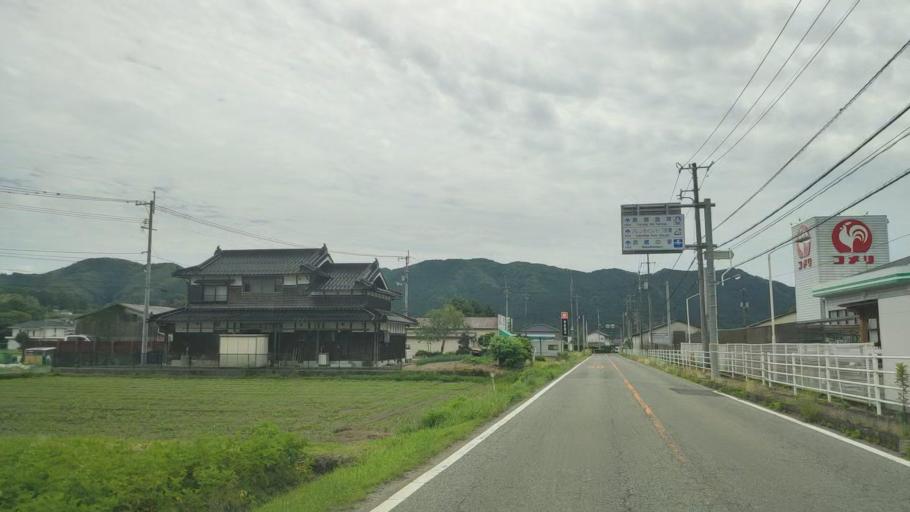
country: JP
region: Hyogo
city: Yamazakicho-nakabirose
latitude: 35.1053
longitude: 134.3256
